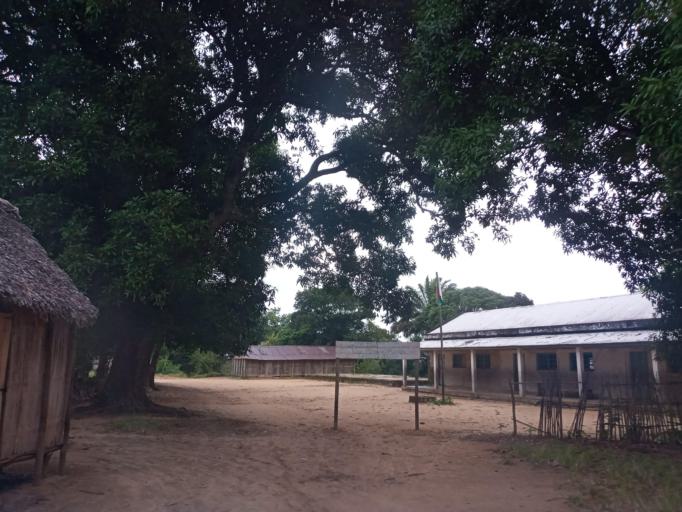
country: MG
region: Atsimo-Atsinanana
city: Vohipaho
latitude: -24.0443
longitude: 47.4393
